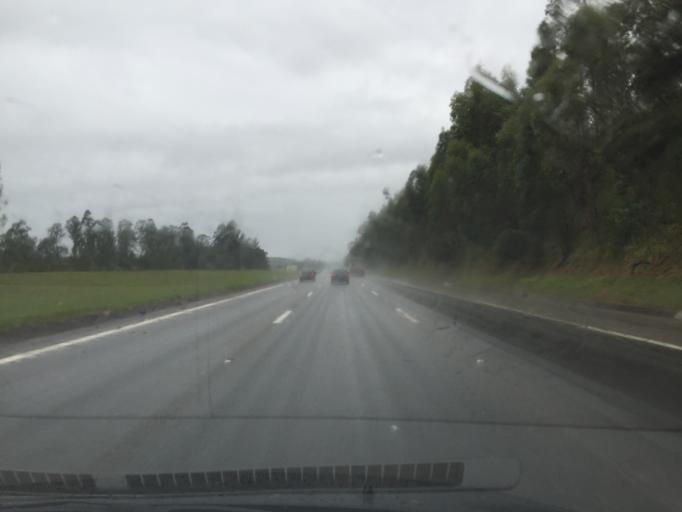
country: BR
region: Sao Paulo
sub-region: Sao Roque
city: Sao Roque
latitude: -23.4217
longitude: -47.1726
